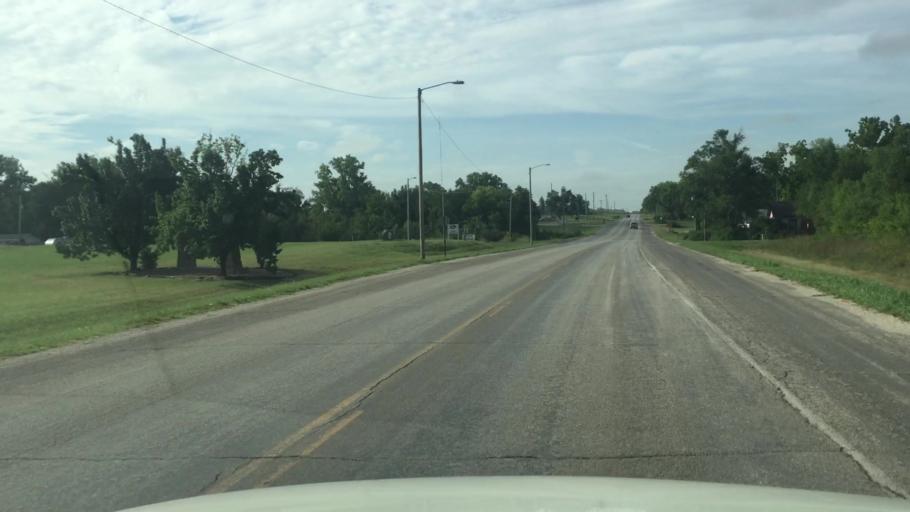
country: US
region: Kansas
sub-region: Allen County
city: Iola
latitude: 37.9017
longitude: -95.4094
